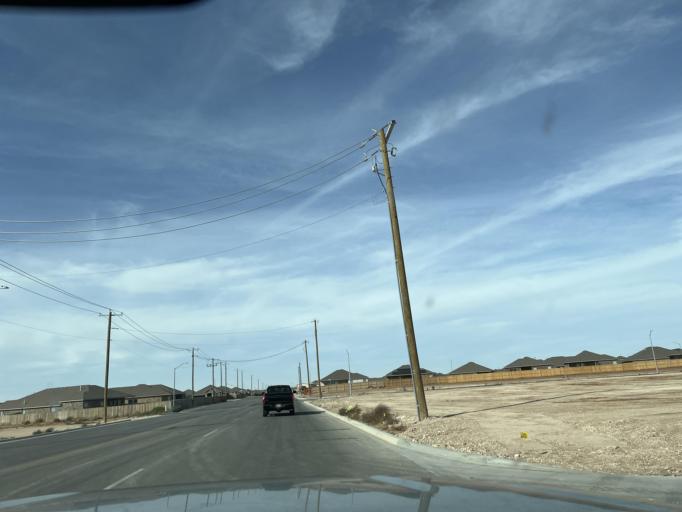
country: US
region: Texas
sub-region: Ector County
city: Gardendale
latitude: 31.9401
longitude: -102.3836
